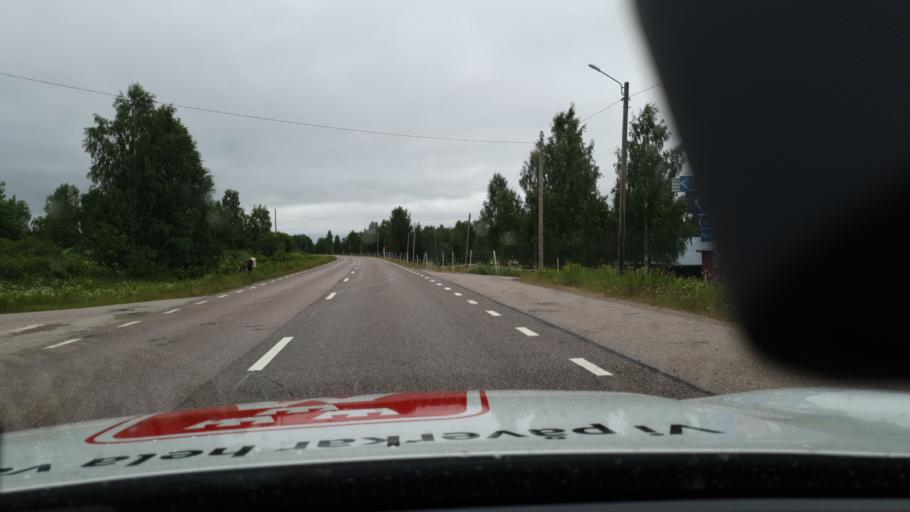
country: FI
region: Lapland
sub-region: Torniolaakso
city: Pello
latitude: 66.9526
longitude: 23.8452
